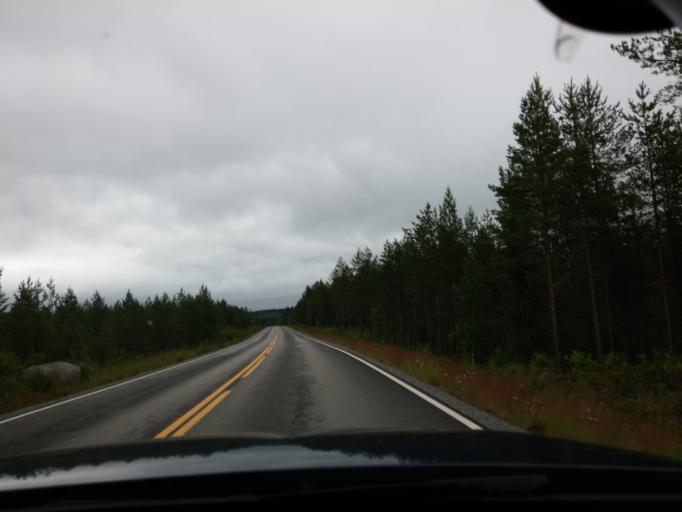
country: FI
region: Central Finland
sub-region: Saarijaervi-Viitasaari
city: Pylkoenmaeki
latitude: 62.6402
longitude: 24.8559
